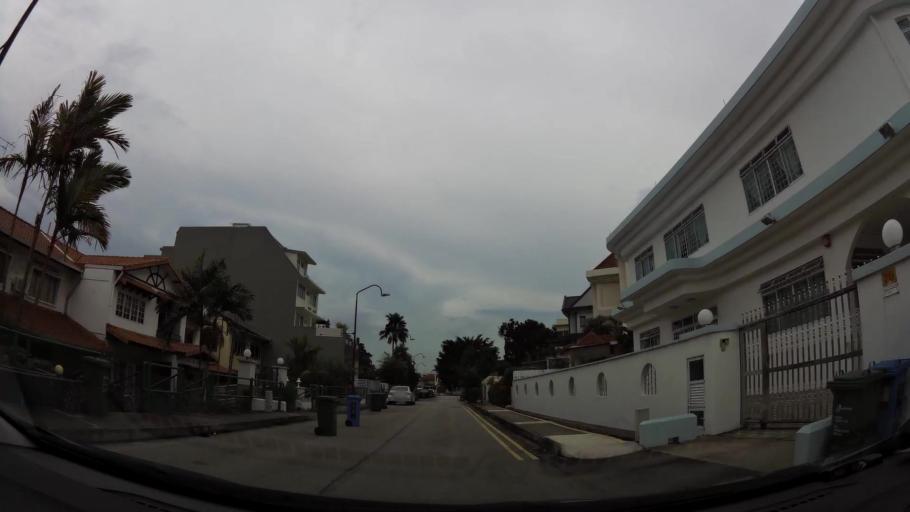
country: SG
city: Singapore
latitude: 1.3643
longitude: 103.8757
